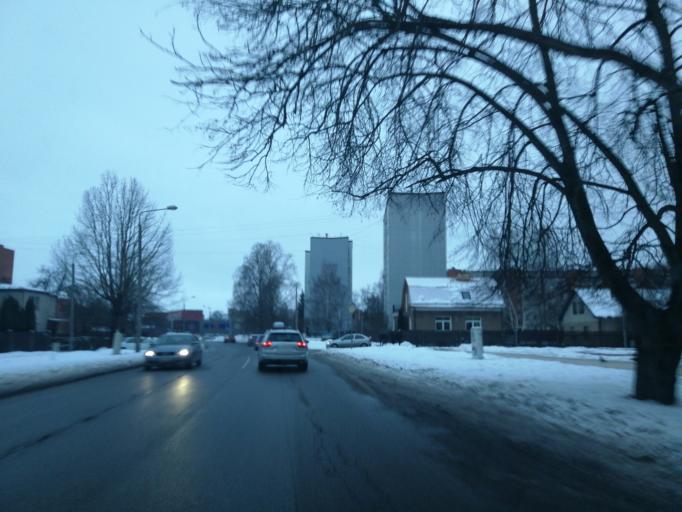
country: LV
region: Riga
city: Riga
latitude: 56.9474
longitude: 24.1719
